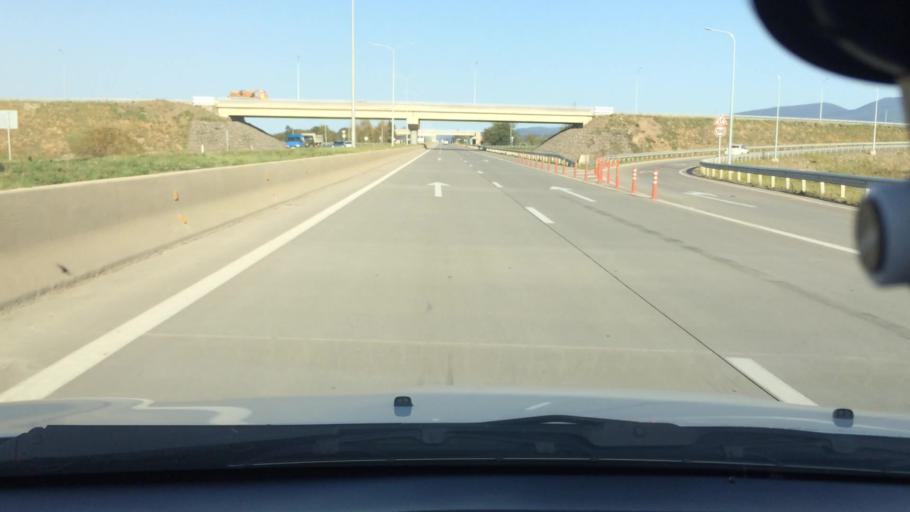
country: GE
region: Imereti
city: Zestap'oni
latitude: 42.1580
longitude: 42.9517
